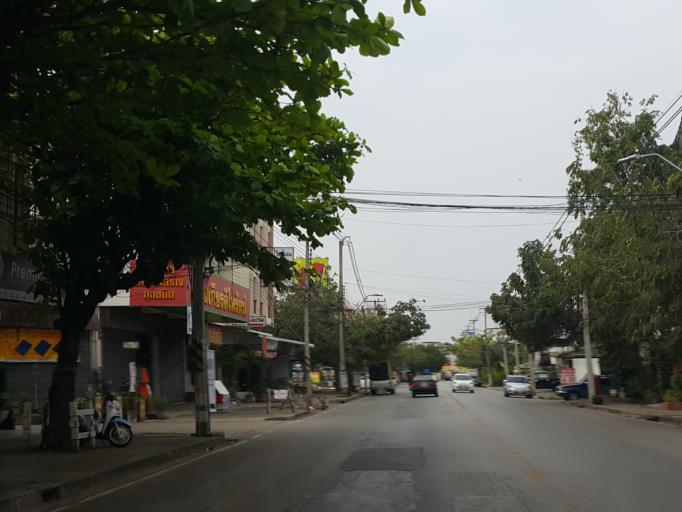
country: TH
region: Lampang
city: Lampang
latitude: 18.2794
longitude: 99.4810
